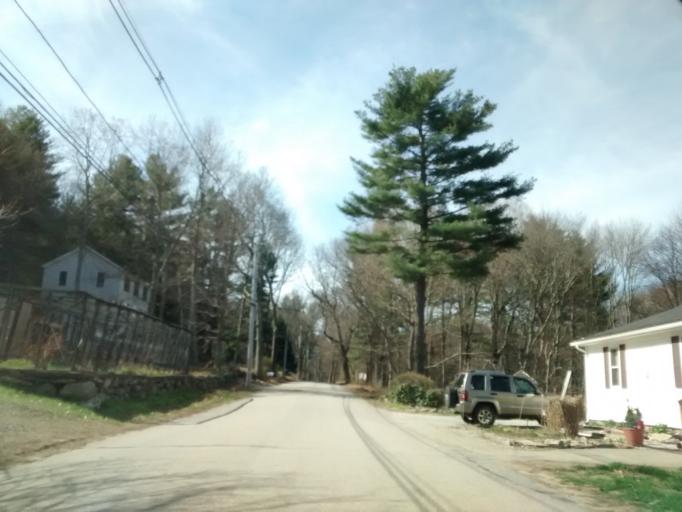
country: US
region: Massachusetts
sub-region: Worcester County
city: Millbury
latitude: 42.1746
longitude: -71.7275
